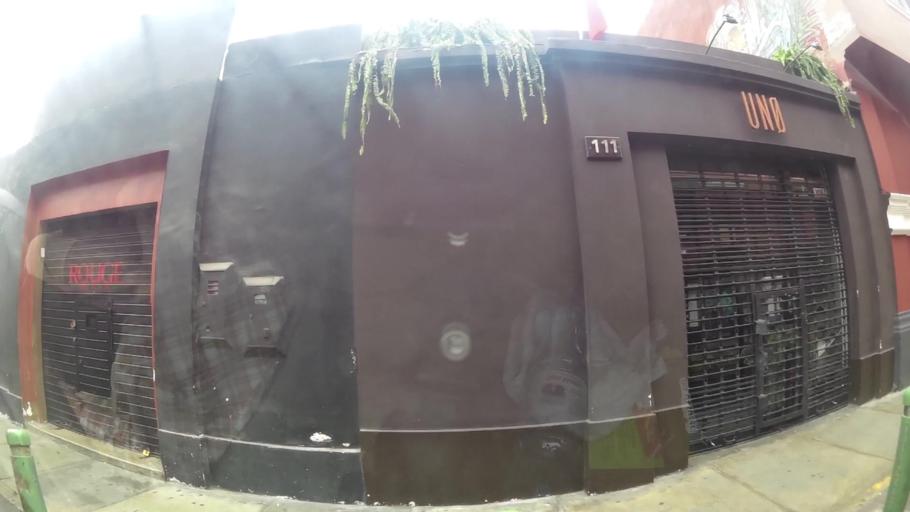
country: PE
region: Lima
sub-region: Lima
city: San Isidro
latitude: -12.1198
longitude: -77.0284
